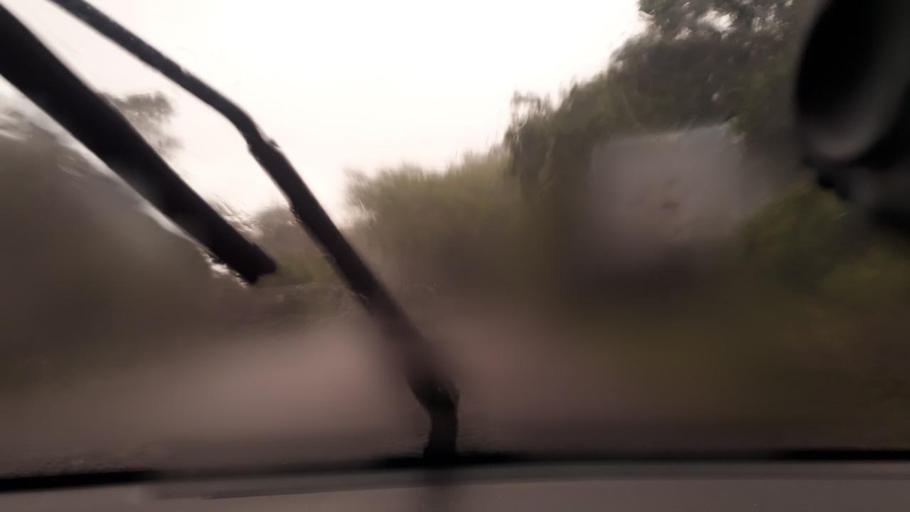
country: GT
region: Jutiapa
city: Comapa
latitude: 14.0341
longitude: -89.9126
